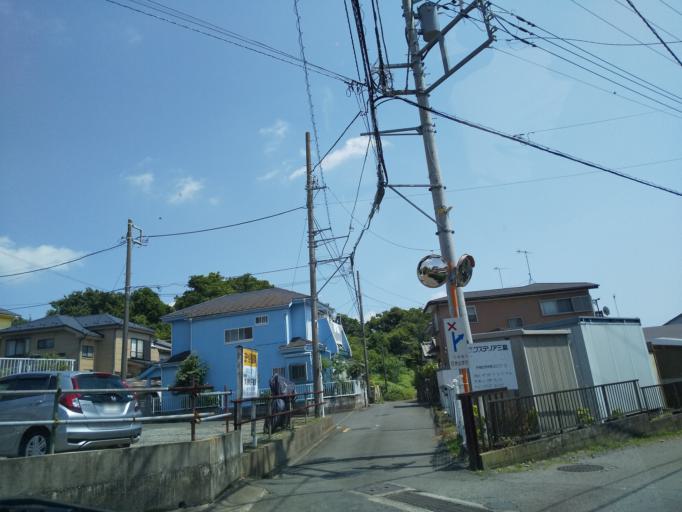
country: JP
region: Kanagawa
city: Zama
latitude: 35.5037
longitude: 139.3908
